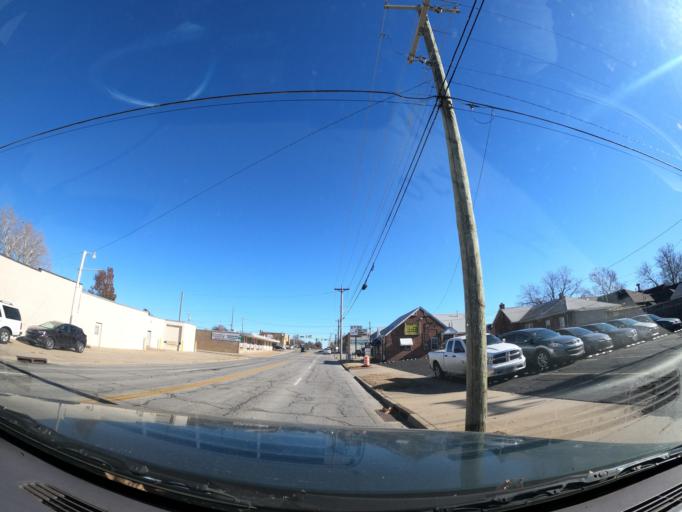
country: US
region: Oklahoma
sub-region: Tulsa County
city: Tulsa
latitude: 36.1405
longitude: -95.9421
